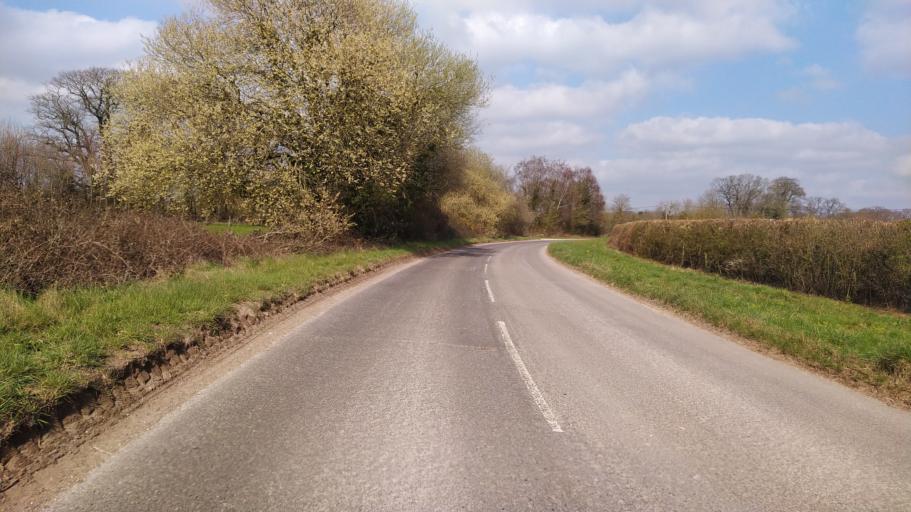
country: GB
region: England
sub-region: Hampshire
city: West Wellow
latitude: 50.9847
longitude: -1.5583
